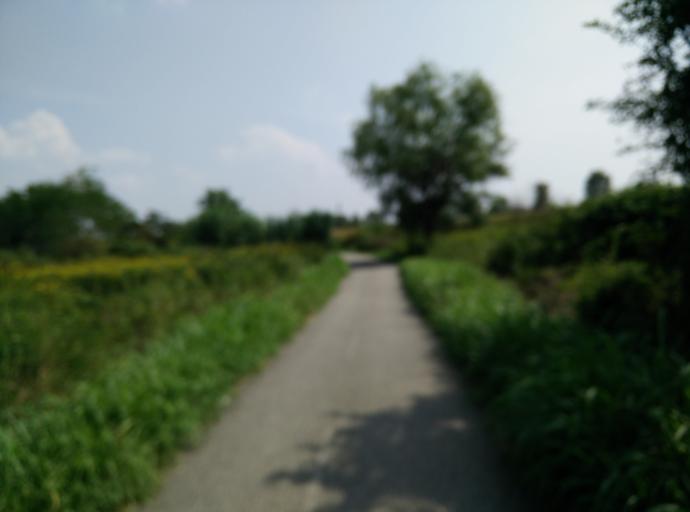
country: IT
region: Piedmont
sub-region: Provincia di Torino
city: Orbassano
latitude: 45.0163
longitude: 7.5376
